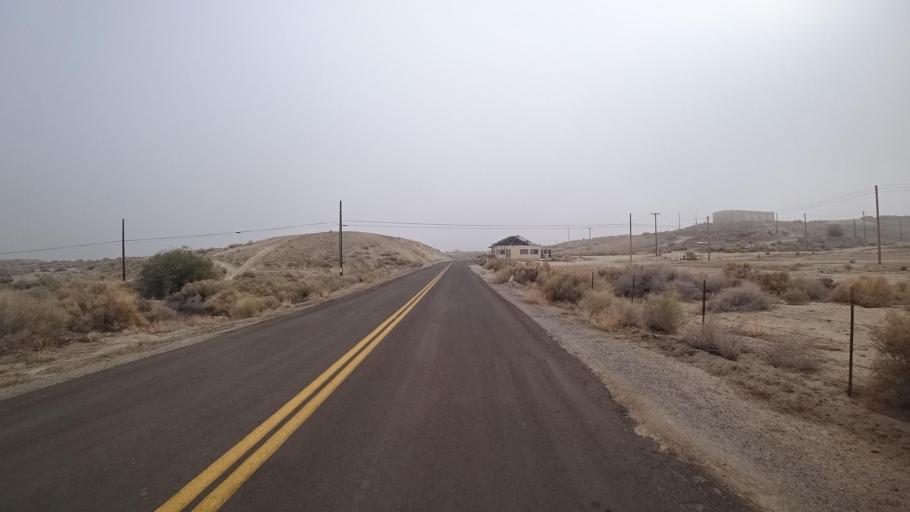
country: US
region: California
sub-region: Kern County
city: Ford City
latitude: 35.1638
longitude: -119.3810
